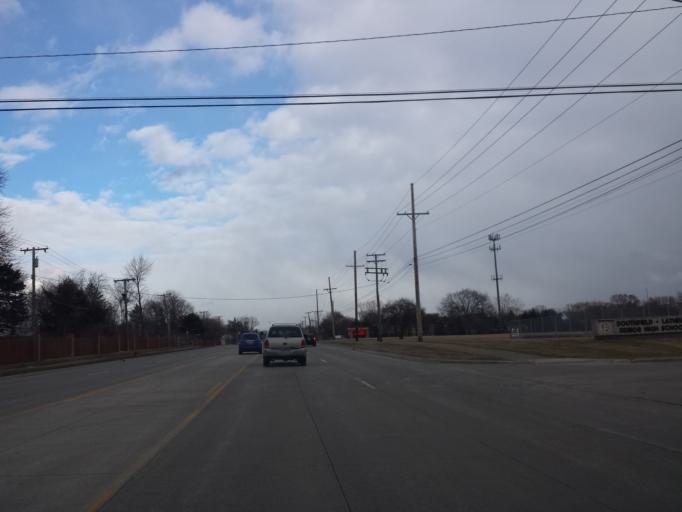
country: US
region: Michigan
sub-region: Oakland County
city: Lathrup Village
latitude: 42.5021
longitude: -83.2372
